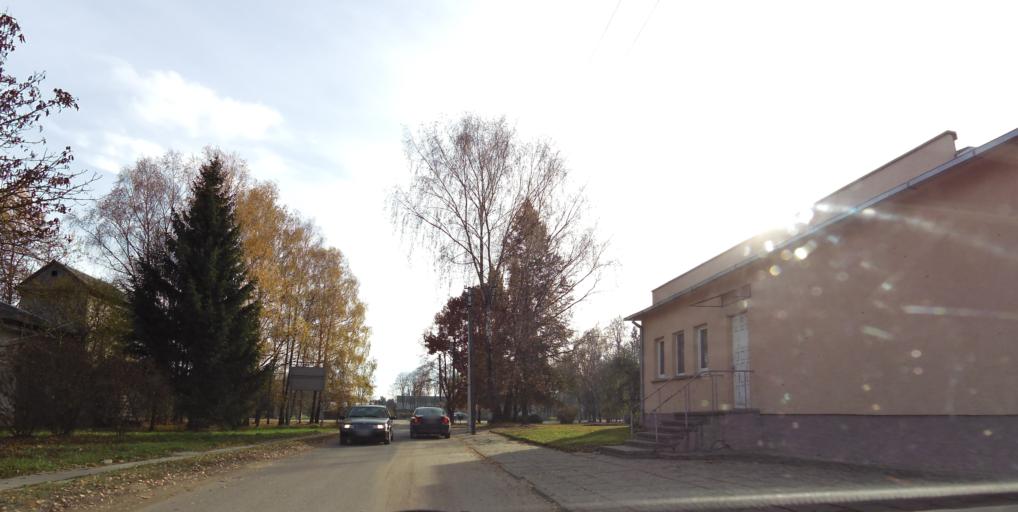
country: LT
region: Vilnius County
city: Pilaite
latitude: 54.7178
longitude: 25.1959
